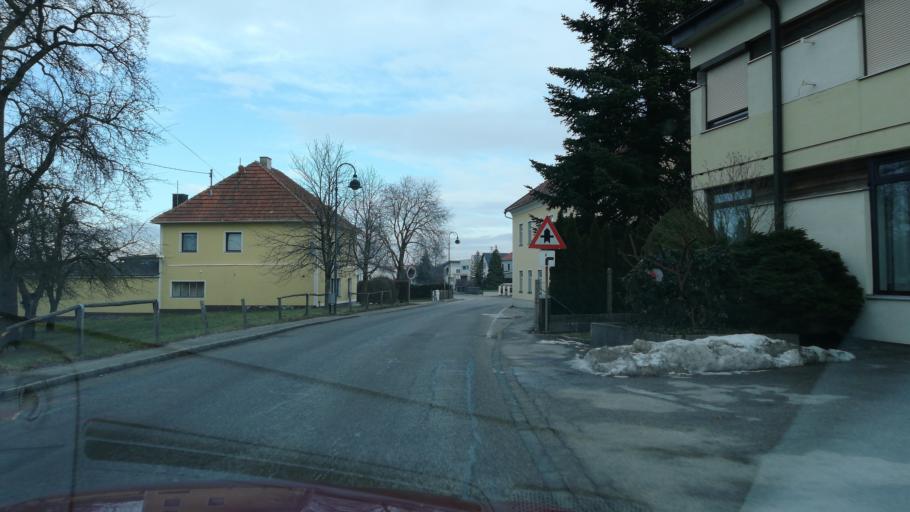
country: AT
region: Upper Austria
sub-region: Politischer Bezirk Vocklabruck
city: Wolfsegg am Hausruck
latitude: 48.1852
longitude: 13.7025
